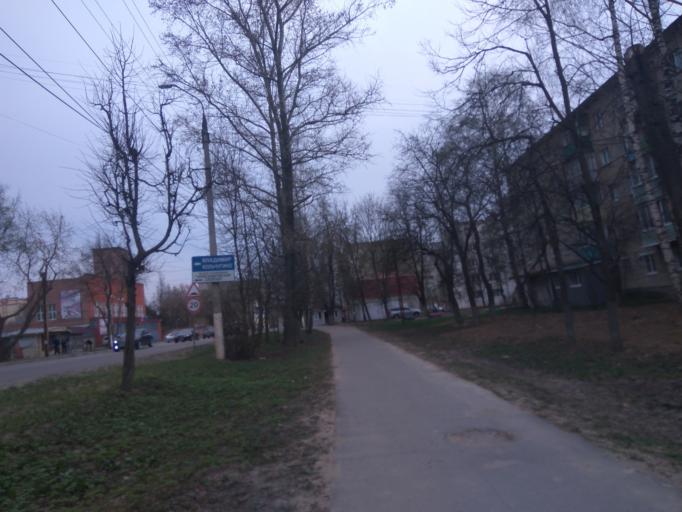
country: RU
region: Vladimir
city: Aleksandrov
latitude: 56.3994
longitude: 38.7136
